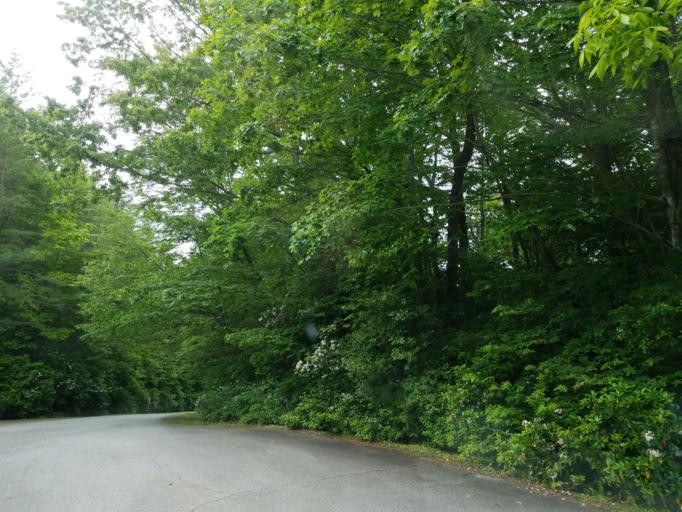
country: US
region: Georgia
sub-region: Union County
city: Blairsville
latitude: 34.7339
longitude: -83.9744
